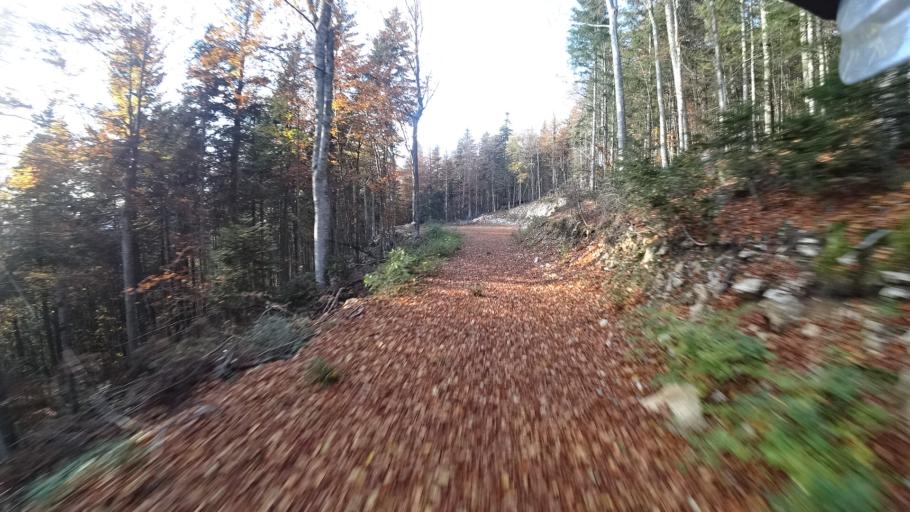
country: HR
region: Karlovacka
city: Plaski
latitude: 44.9558
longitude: 15.3972
